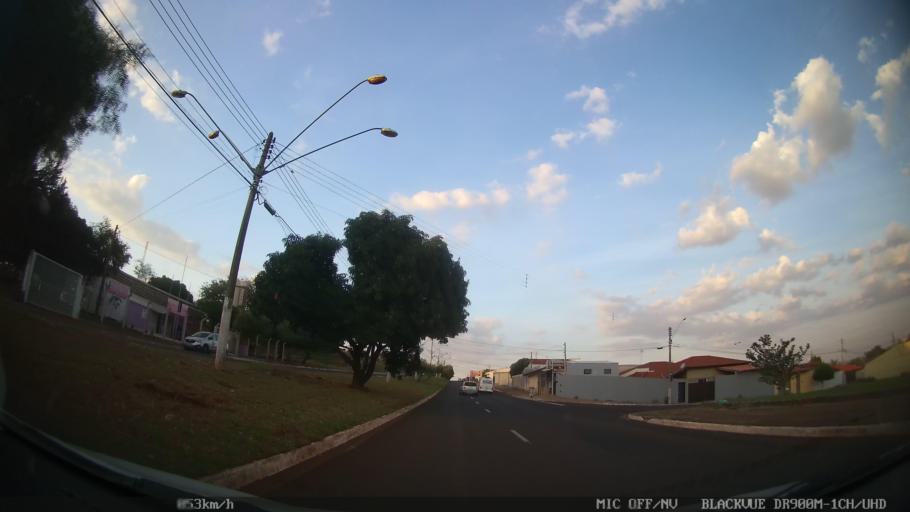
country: BR
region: Sao Paulo
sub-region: Ribeirao Preto
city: Ribeirao Preto
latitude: -21.1385
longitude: -47.8510
